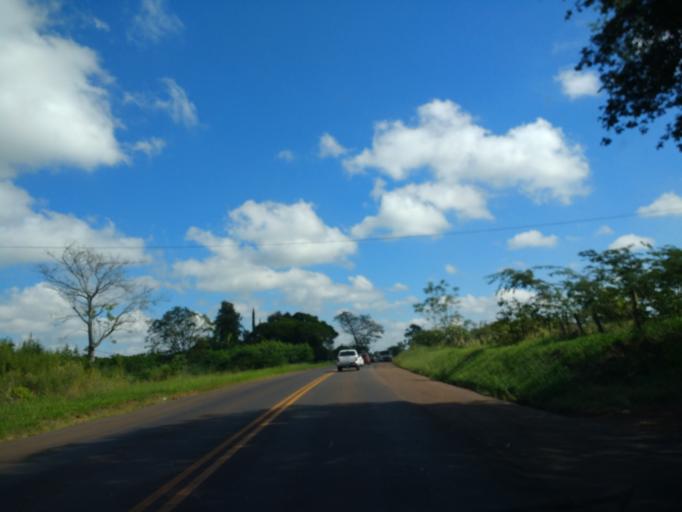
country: BR
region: Parana
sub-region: Umuarama
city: Umuarama
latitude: -23.8238
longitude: -53.3384
